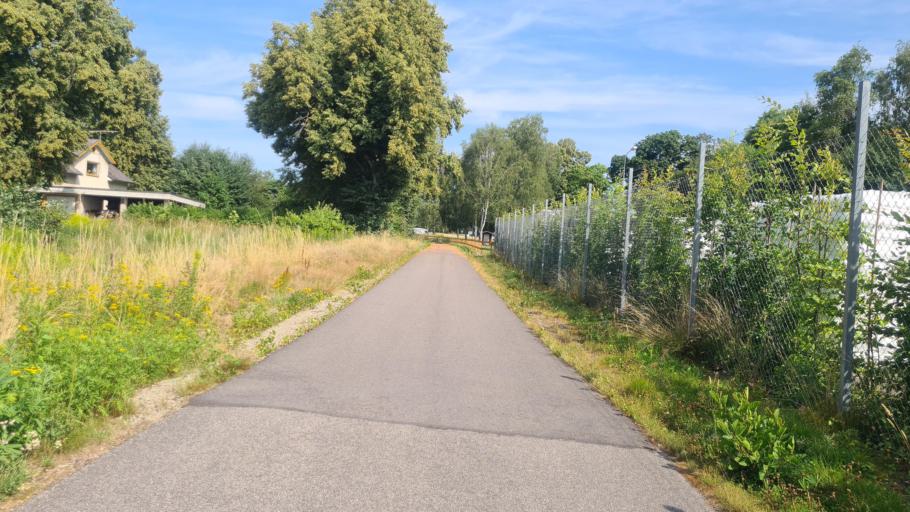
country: SE
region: Kronoberg
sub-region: Ljungby Kommun
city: Lagan
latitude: 56.9161
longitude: 13.9901
